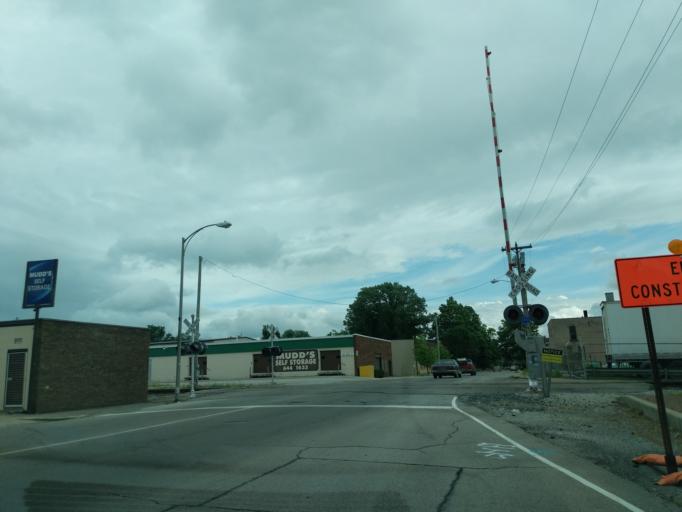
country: US
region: Indiana
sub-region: Madison County
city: Anderson
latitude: 40.1014
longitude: -85.6783
